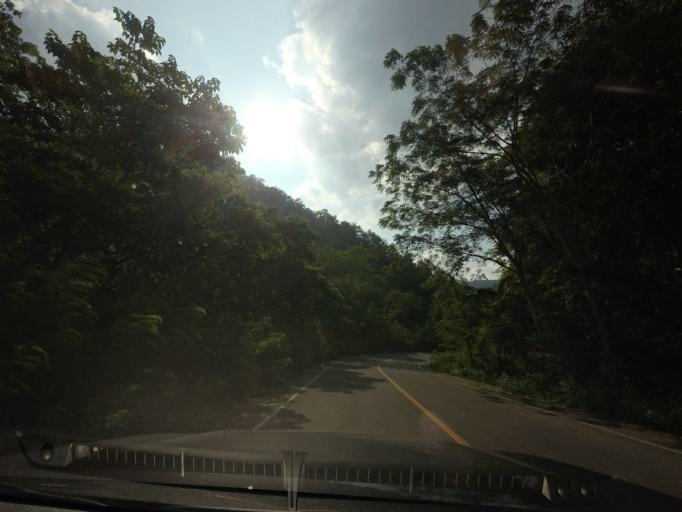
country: TH
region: Nan
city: Na Noi
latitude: 18.3119
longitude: 100.8987
